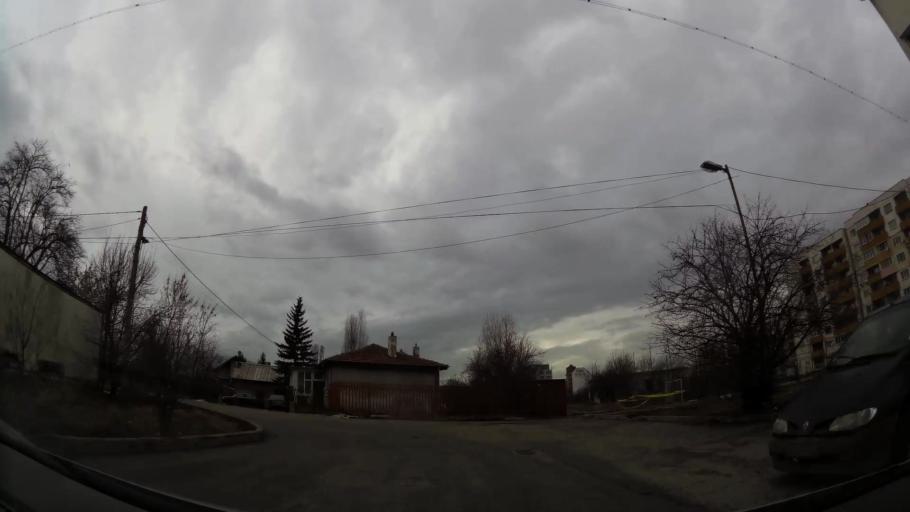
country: BG
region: Sofia-Capital
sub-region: Stolichna Obshtina
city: Sofia
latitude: 42.7228
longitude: 23.2773
